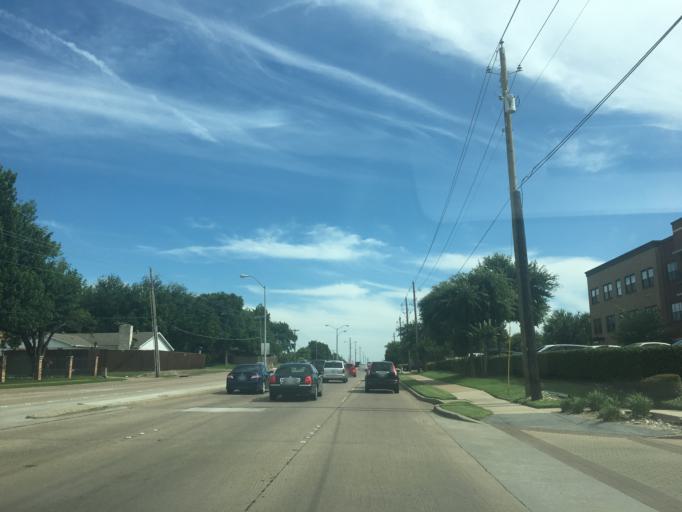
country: US
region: Texas
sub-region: Dallas County
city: Richardson
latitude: 32.9588
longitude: -96.6828
